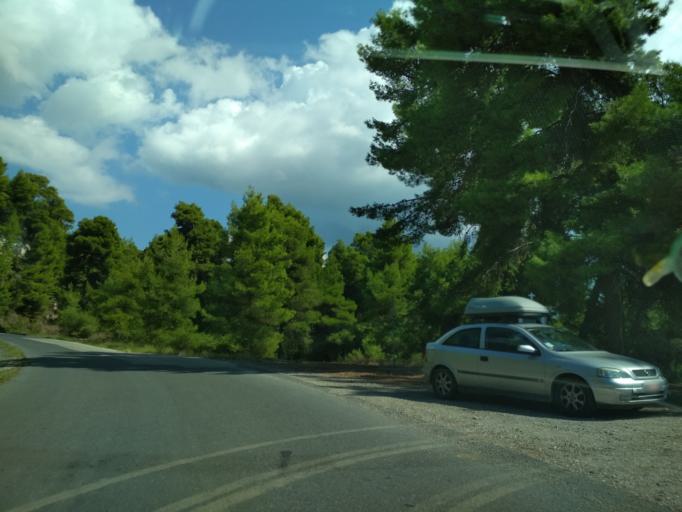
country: GR
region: Central Greece
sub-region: Nomos Evvoias
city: Roviai
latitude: 38.8159
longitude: 23.2761
